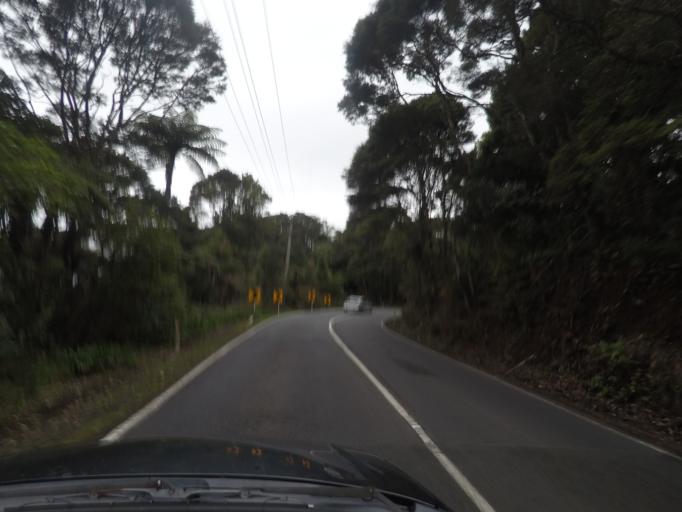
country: NZ
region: Auckland
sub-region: Auckland
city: Titirangi
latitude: -36.9329
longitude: 174.5810
